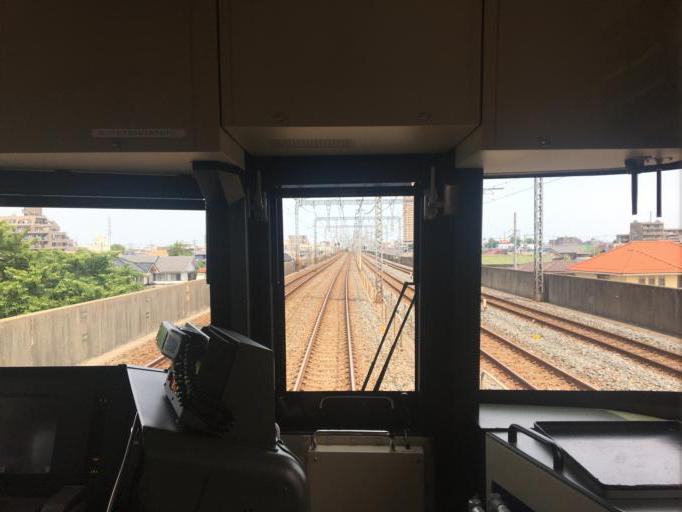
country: JP
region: Saitama
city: Koshigaya
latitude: 35.8952
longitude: 139.7826
